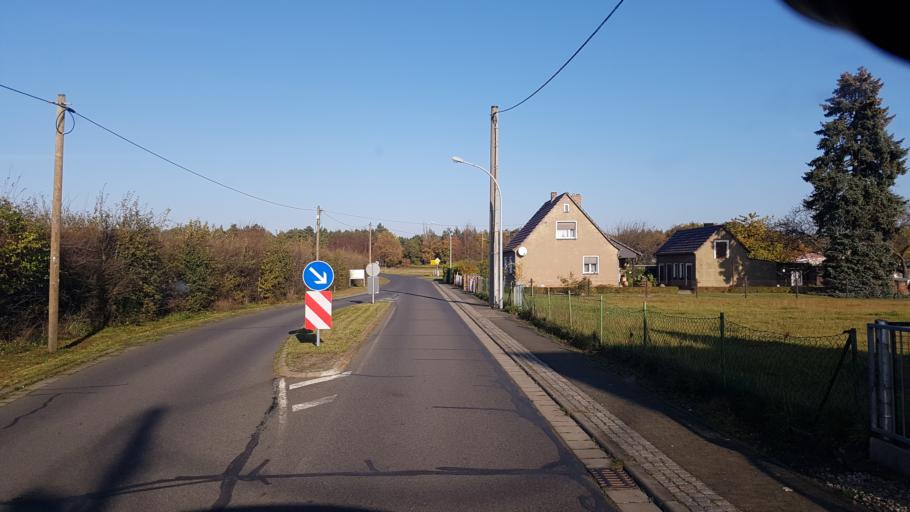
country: DE
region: Brandenburg
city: Schipkau
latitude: 51.5710
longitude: 13.9230
